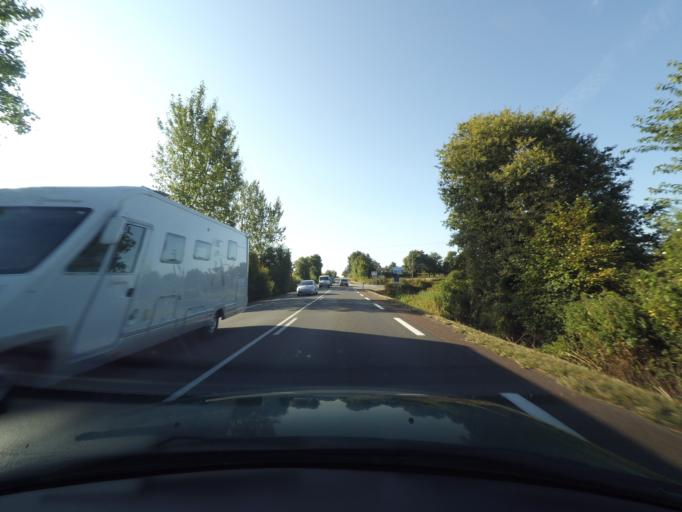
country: FR
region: Poitou-Charentes
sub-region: Departement des Deux-Sevres
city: Viennay
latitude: 46.6766
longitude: -0.2611
